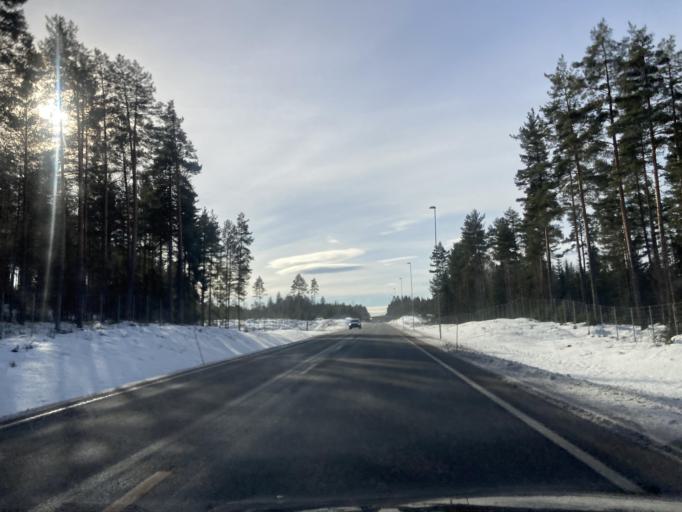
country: NO
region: Hedmark
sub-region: Loten
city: Loten
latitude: 60.7622
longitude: 11.3084
